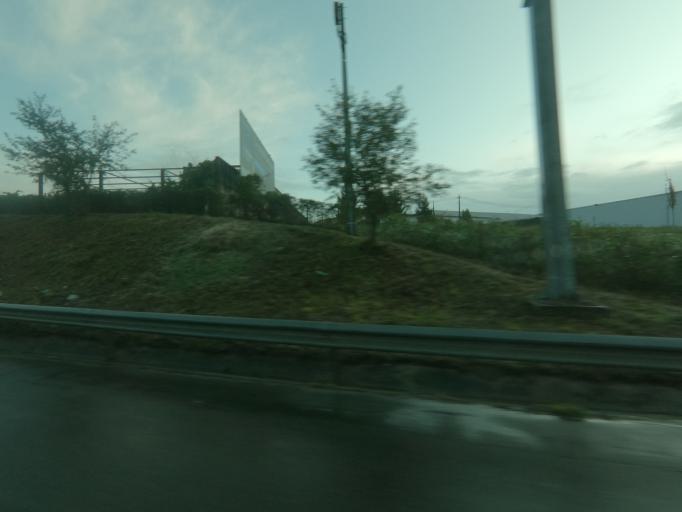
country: PT
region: Viana do Castelo
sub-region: Valenca
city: Valenca
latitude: 42.0236
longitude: -8.6493
